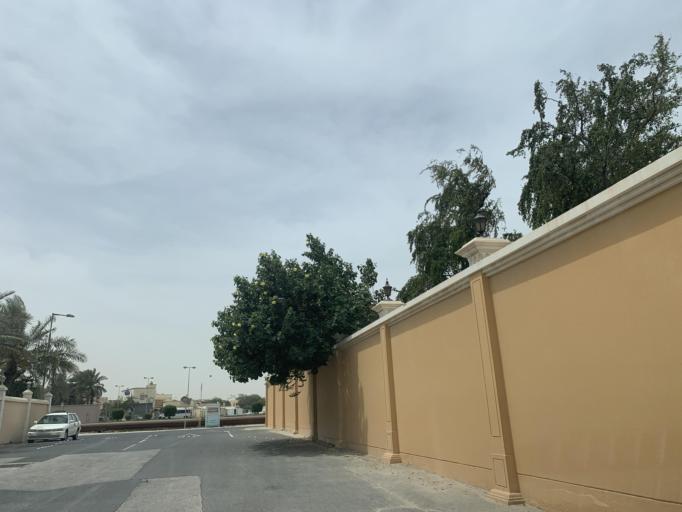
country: BH
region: Northern
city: Ar Rifa'
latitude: 26.1337
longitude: 50.5412
